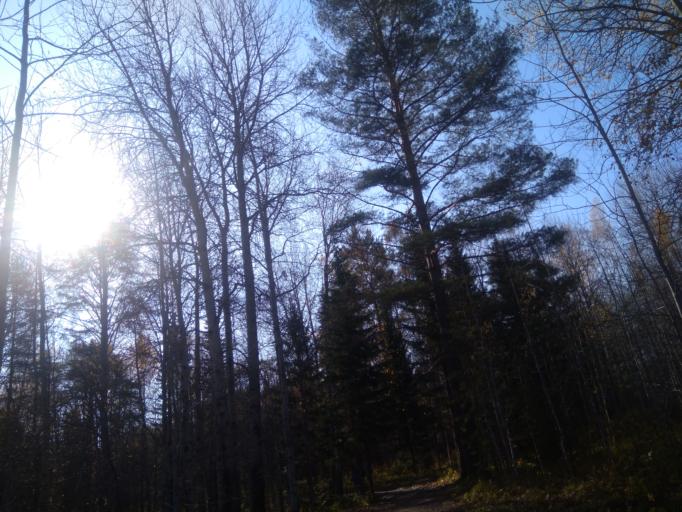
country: RU
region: Sverdlovsk
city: Mikhaylovsk
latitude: 56.5215
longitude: 59.2348
